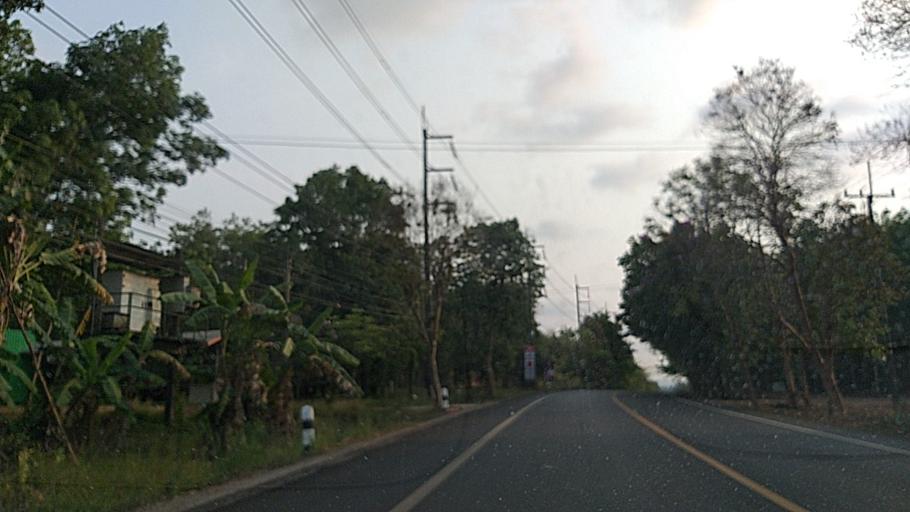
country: TH
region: Trat
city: Khao Saming
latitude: 12.3506
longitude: 102.3800
